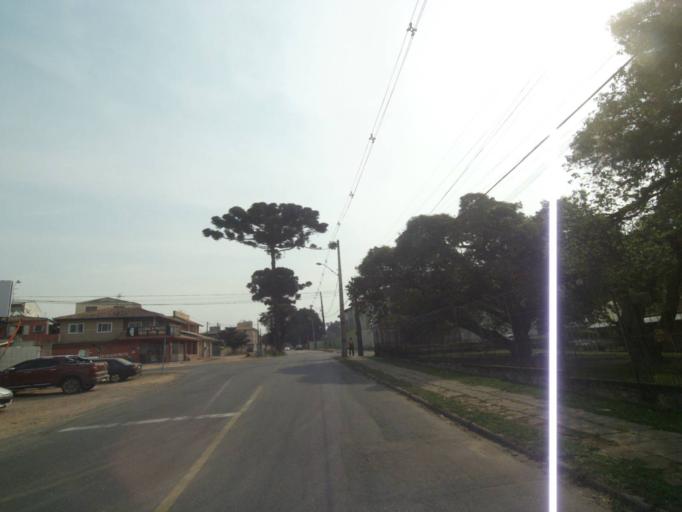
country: BR
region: Parana
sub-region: Sao Jose Dos Pinhais
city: Sao Jose dos Pinhais
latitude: -25.5259
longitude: -49.2735
